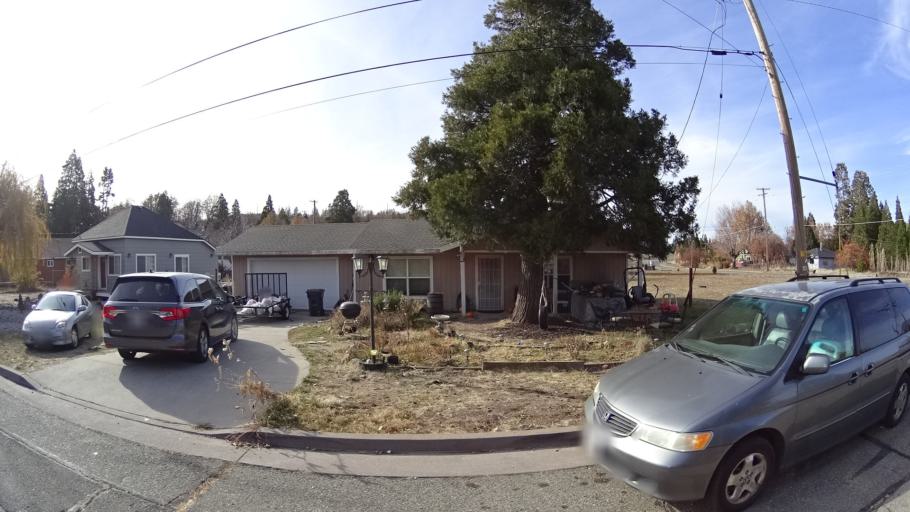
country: US
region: California
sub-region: Siskiyou County
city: Weed
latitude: 41.4354
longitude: -122.3847
